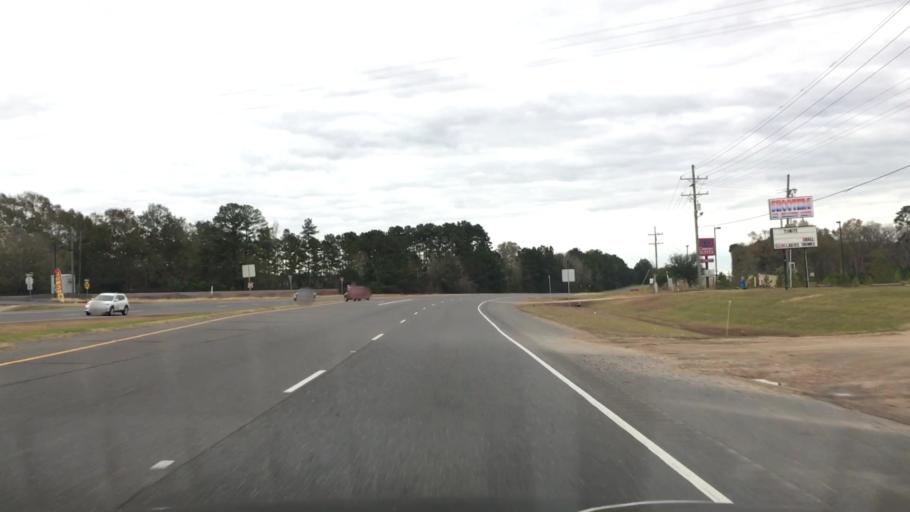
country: US
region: Louisiana
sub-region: Vernon Parish
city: New Llano
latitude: 31.1009
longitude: -93.2695
